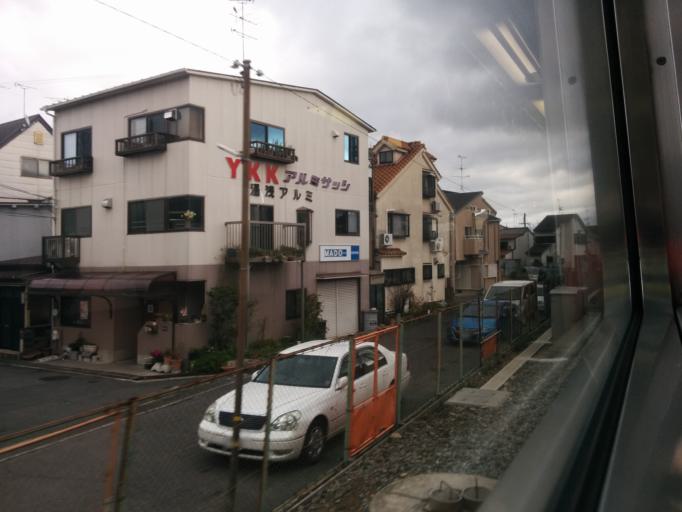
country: JP
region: Kyoto
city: Muko
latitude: 34.9594
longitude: 135.7036
